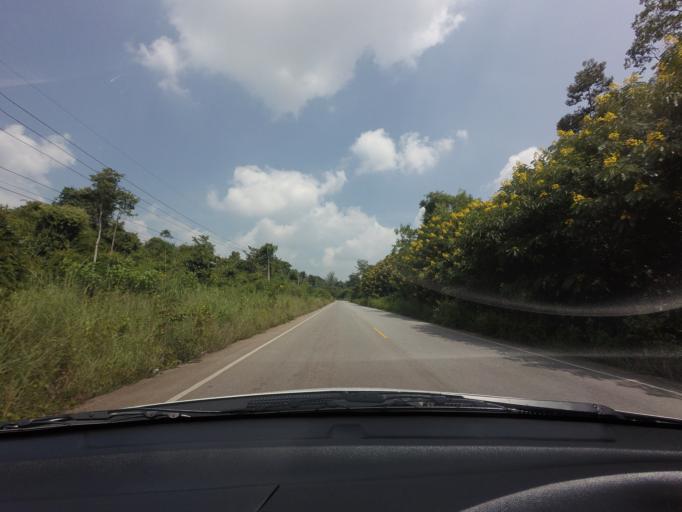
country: TH
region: Nakhon Ratchasima
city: Pak Chong
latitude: 14.5963
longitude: 101.5726
